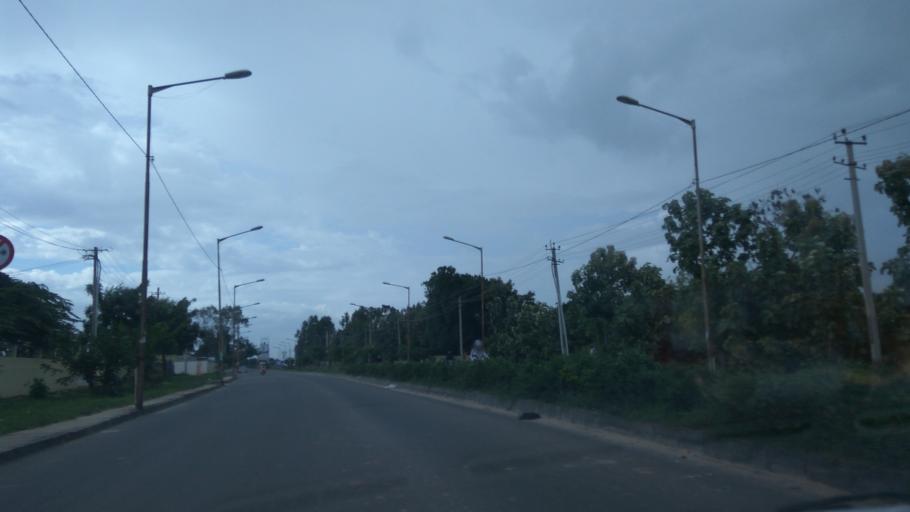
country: IN
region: Karnataka
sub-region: Bangalore Urban
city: Yelahanka
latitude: 13.0985
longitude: 77.6357
